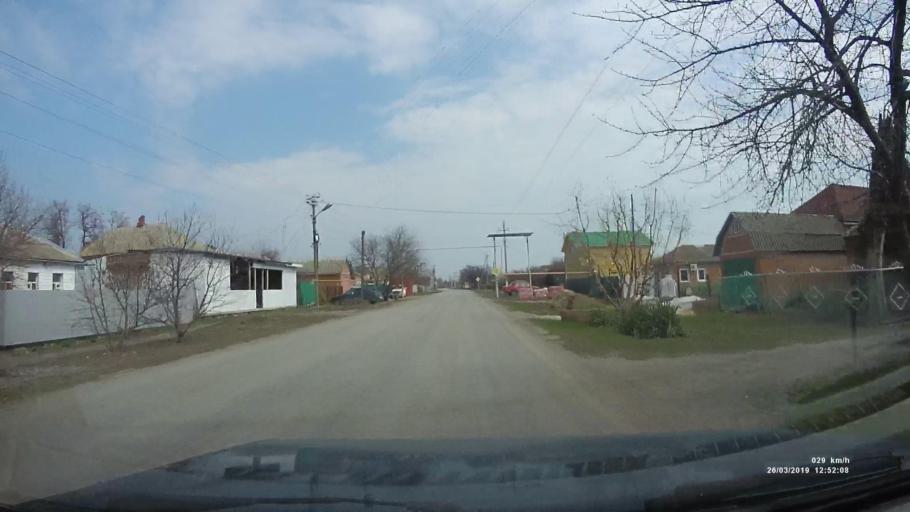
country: RU
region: Rostov
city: Novobessergenovka
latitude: 47.1592
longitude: 38.7107
